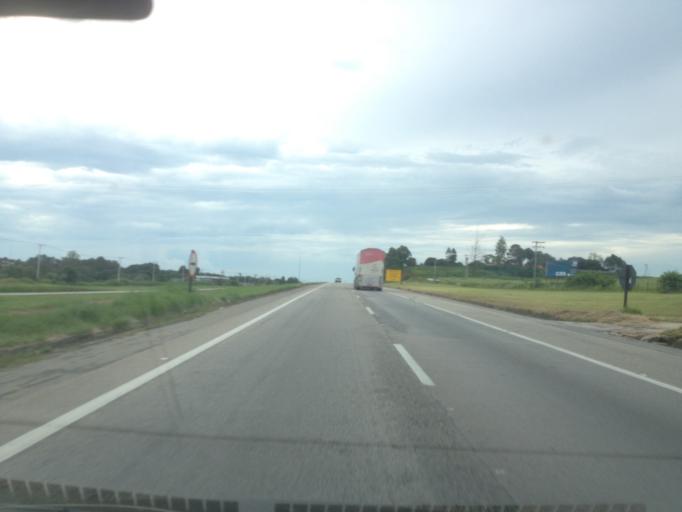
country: BR
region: Sao Paulo
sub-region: Sorocaba
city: Sorocaba
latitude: -23.3713
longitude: -47.4492
